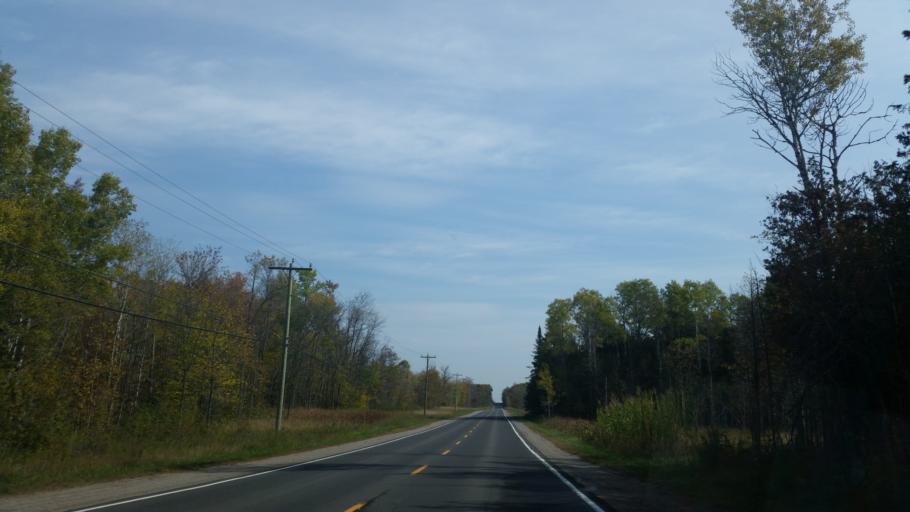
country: CA
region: Ontario
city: Orillia
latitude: 44.6370
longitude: -79.1809
